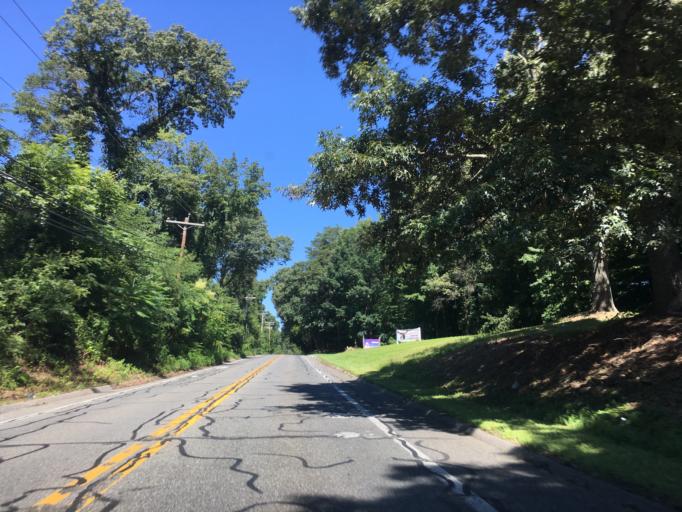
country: US
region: Maryland
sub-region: Anne Arundel County
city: Crownsville
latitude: 39.0564
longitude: -76.6235
